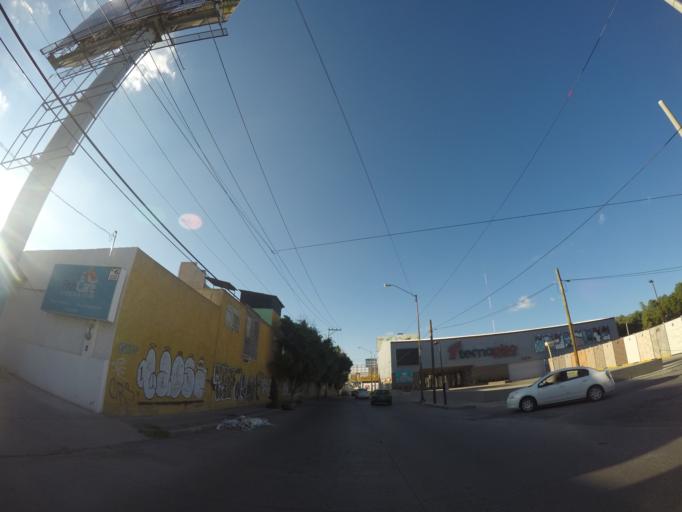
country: MX
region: San Luis Potosi
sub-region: San Luis Potosi
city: San Luis Potosi
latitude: 22.1567
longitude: -100.9999
